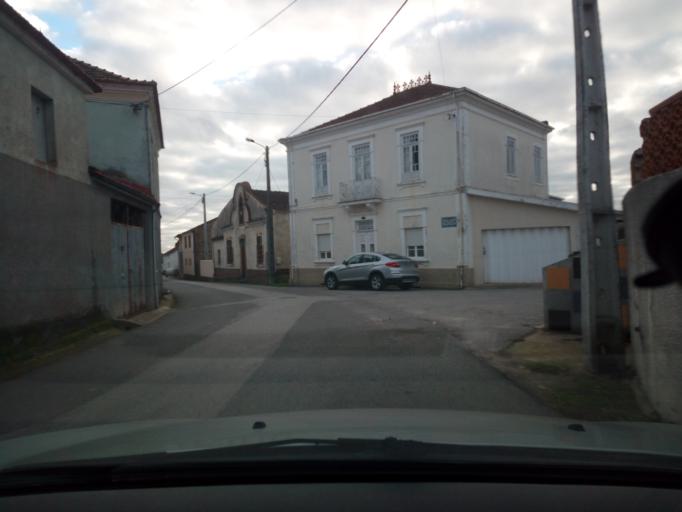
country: PT
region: Aveiro
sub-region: Oliveira do Bairro
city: Oliveira do Bairro
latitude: 40.5483
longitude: -8.4888
